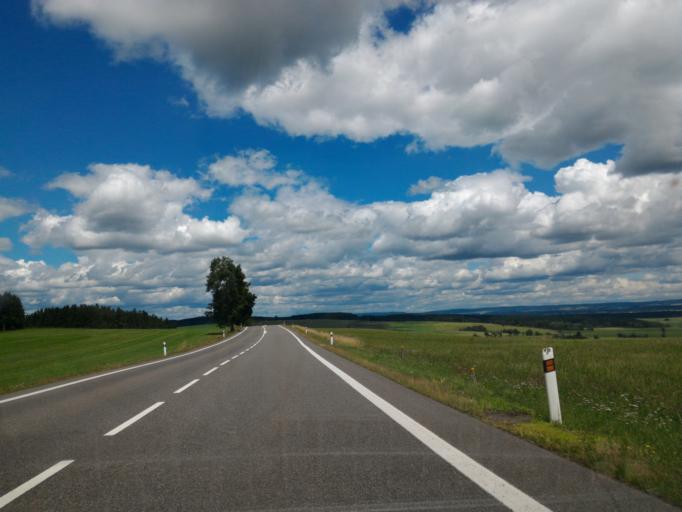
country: CZ
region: Vysocina
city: Bohdalov
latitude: 49.4672
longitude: 15.8247
